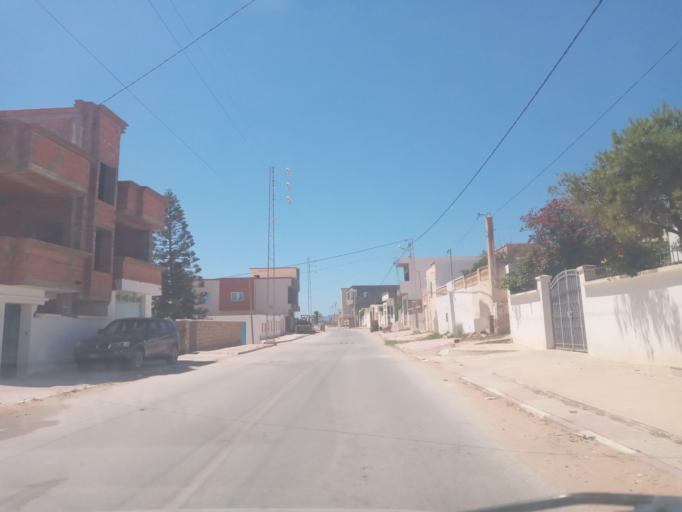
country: TN
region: Nabul
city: El Haouaria
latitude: 37.0502
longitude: 11.0021
